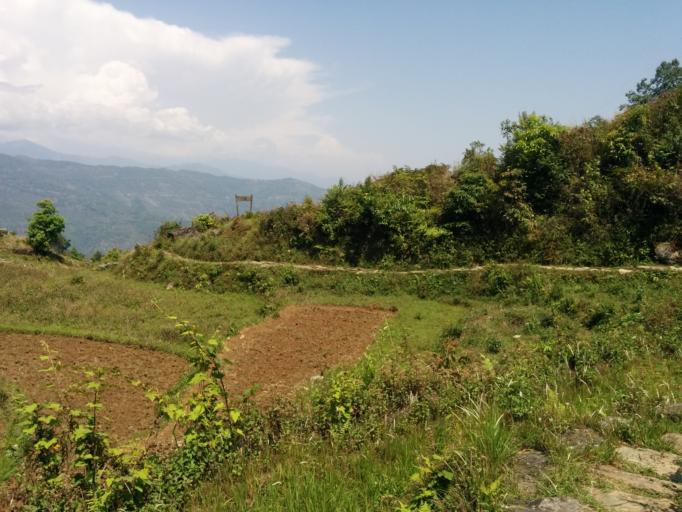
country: NP
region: Western Region
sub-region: Gandaki Zone
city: Pokhara
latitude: 28.2288
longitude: 83.8513
